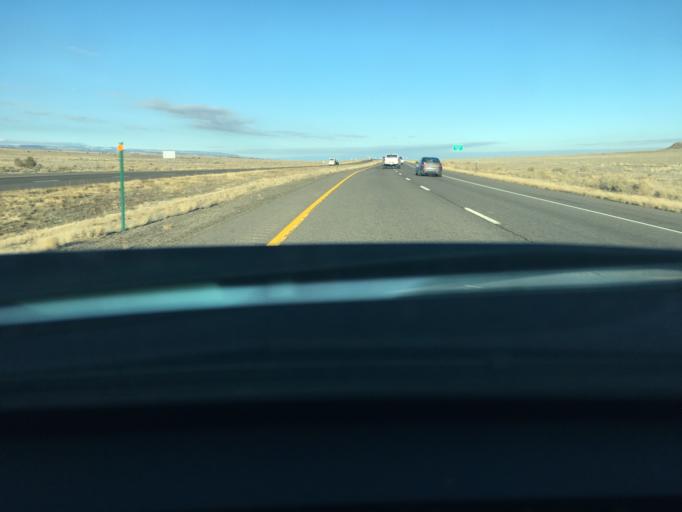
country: US
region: Colorado
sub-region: Delta County
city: Delta
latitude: 38.7816
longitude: -108.2420
